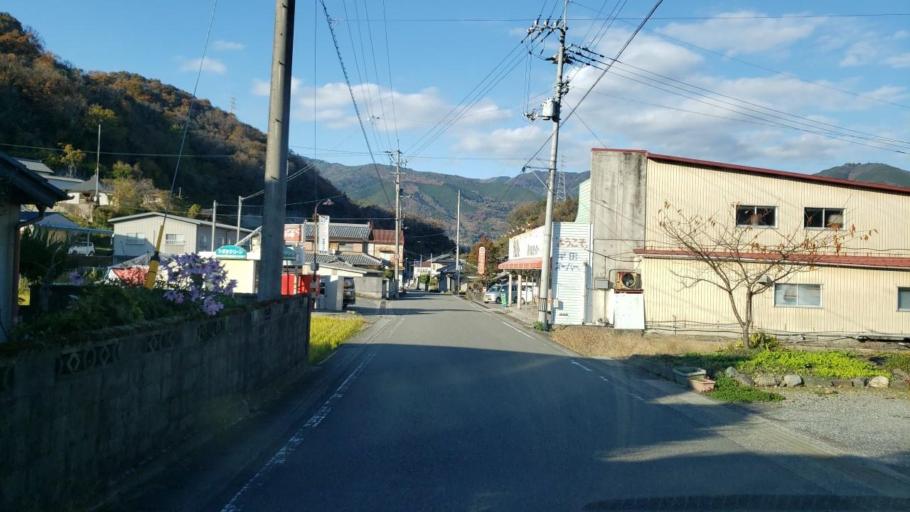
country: JP
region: Tokushima
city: Wakimachi
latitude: 34.0349
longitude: 134.0287
